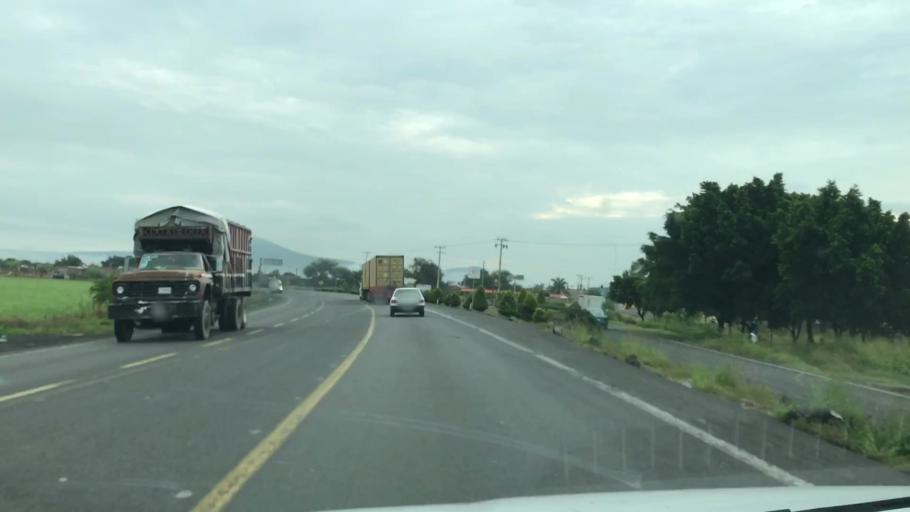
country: MX
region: Michoacan
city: Tanhuato de Guerrero
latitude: 20.2841
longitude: -102.3415
